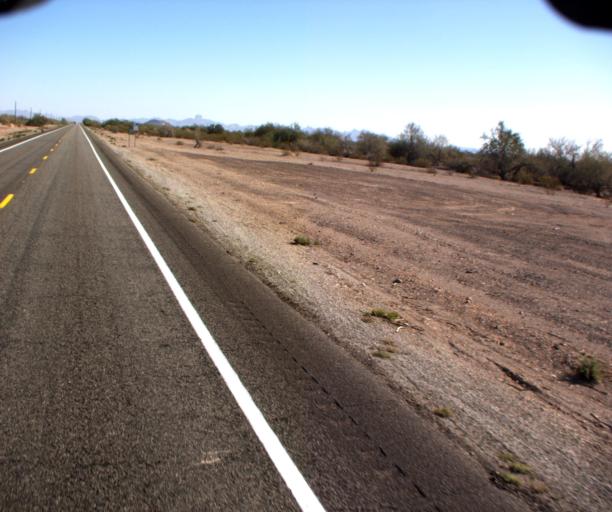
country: US
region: Arizona
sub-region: Yuma County
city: Fortuna Foothills
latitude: 32.8868
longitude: -114.3426
